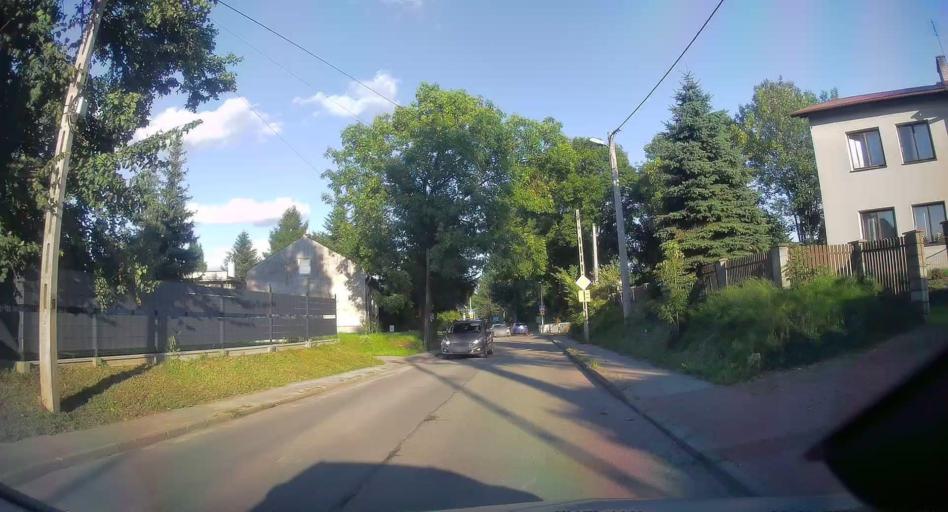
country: PL
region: Lesser Poland Voivodeship
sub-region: Powiat wielicki
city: Czarnochowice
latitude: 50.0169
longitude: 20.0480
